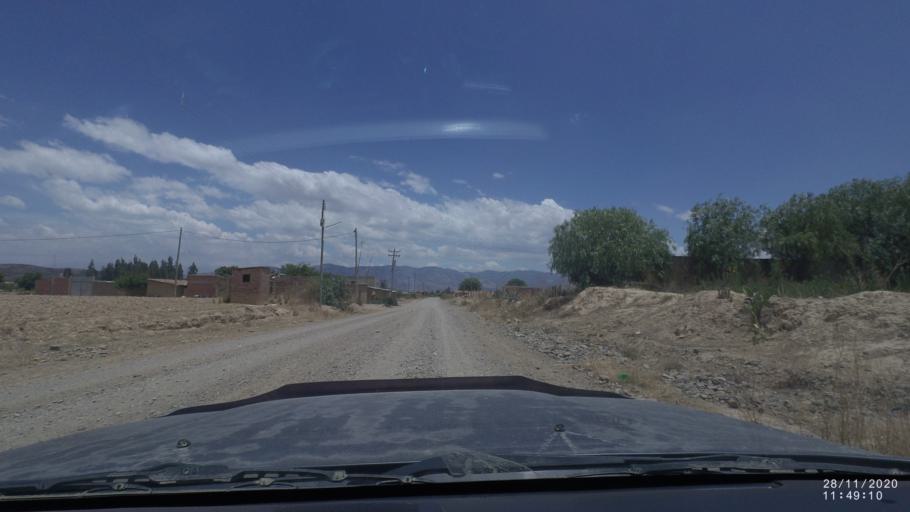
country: BO
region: Cochabamba
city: Tarata
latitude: -17.6338
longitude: -66.0299
